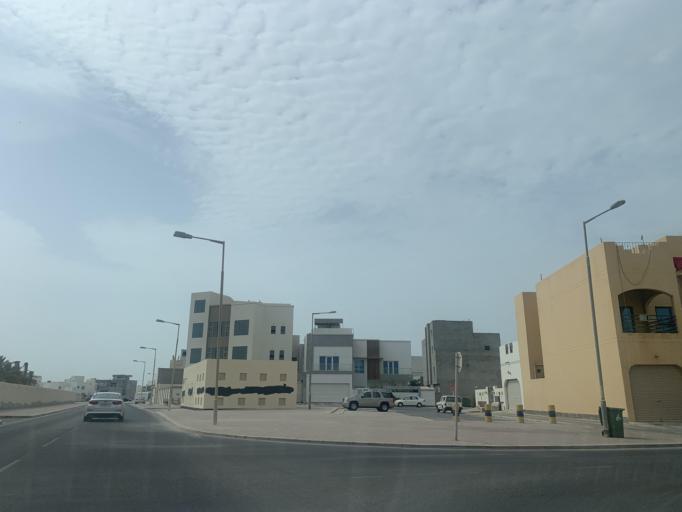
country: BH
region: Muharraq
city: Al Muharraq
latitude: 26.2846
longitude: 50.6358
